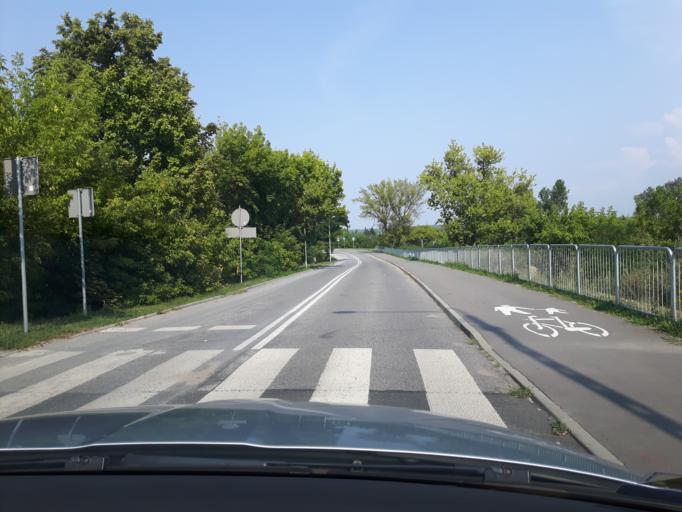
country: PL
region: Masovian Voivodeship
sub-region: Powiat nowodworski
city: Nowy Dwor Mazowiecki
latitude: 52.4412
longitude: 20.6969
